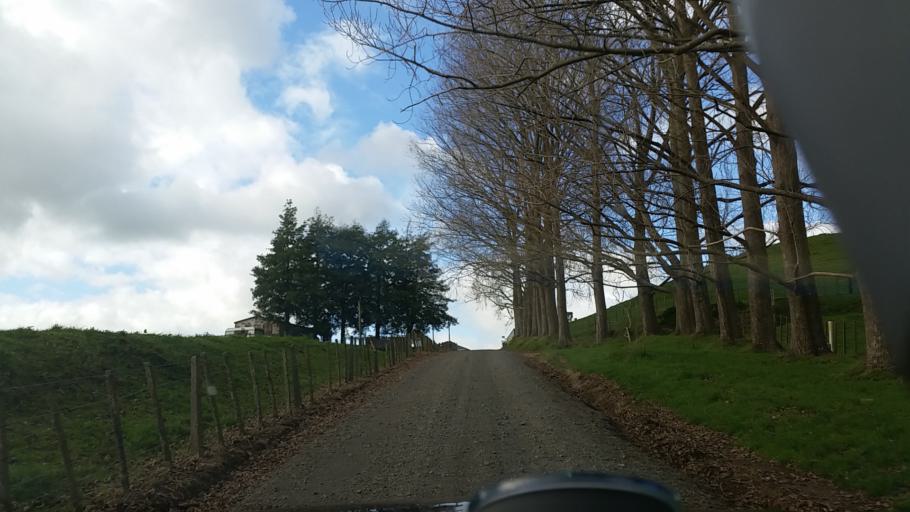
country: NZ
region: Waikato
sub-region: Matamata-Piako District
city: Matamata
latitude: -37.8249
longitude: 175.6763
